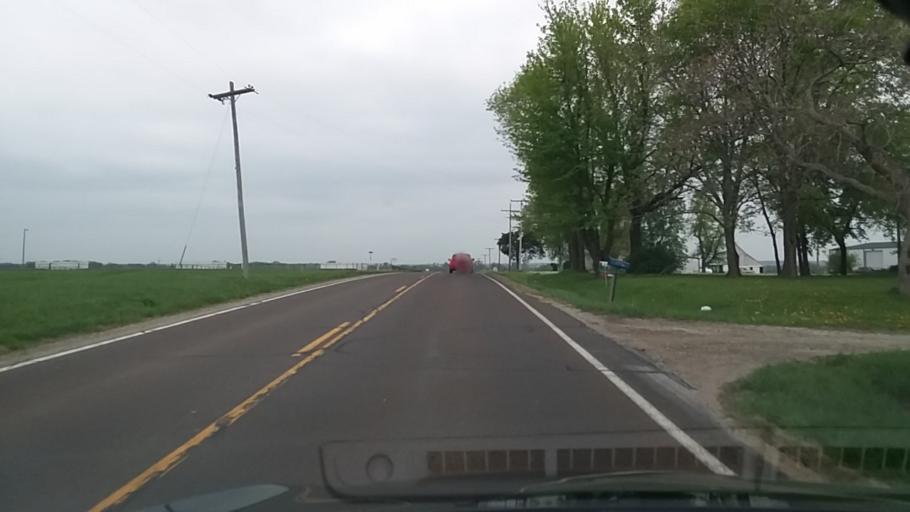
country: US
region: Kansas
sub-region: Douglas County
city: Eudora
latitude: 38.8997
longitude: -95.0934
